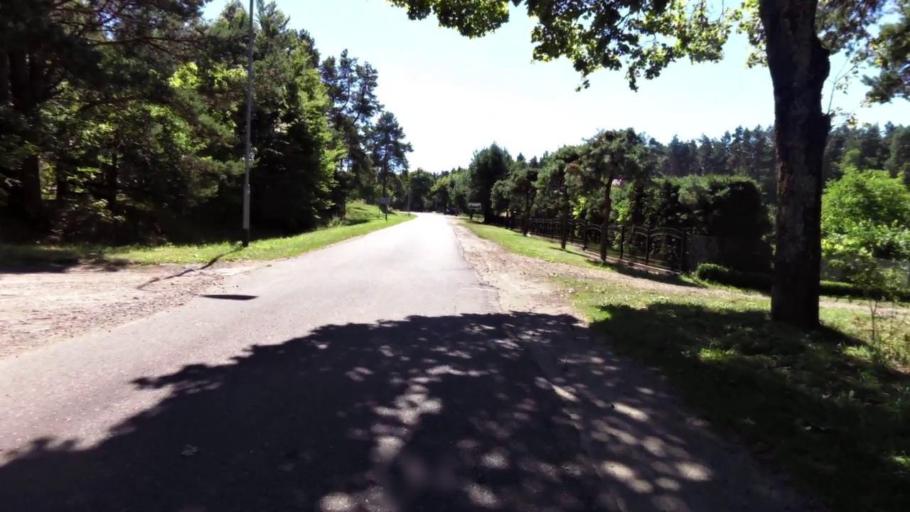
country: PL
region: West Pomeranian Voivodeship
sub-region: Powiat szczecinecki
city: Bialy Bor
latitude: 53.9072
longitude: 16.8334
